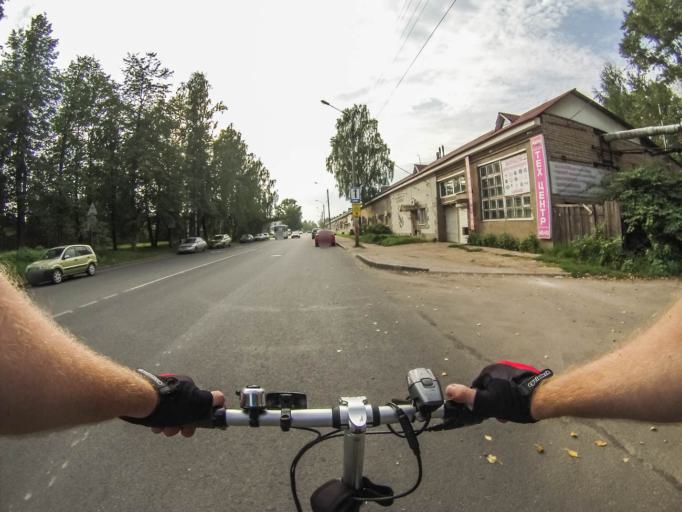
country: RU
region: Kostroma
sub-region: Kostromskoy Rayon
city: Kostroma
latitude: 57.7823
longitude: 40.8862
